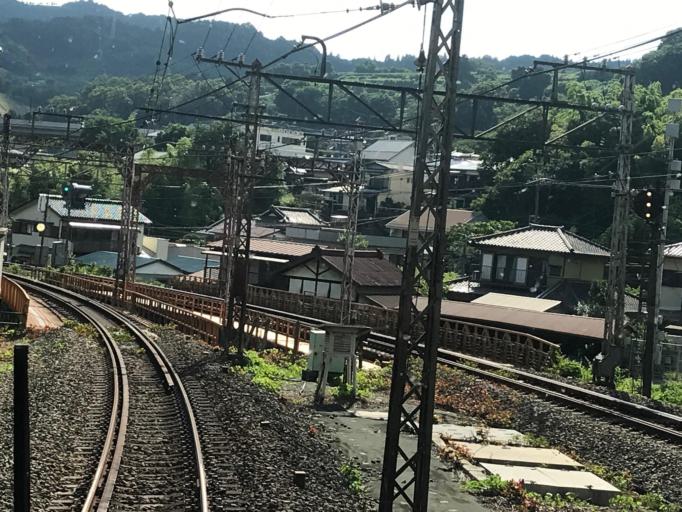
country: JP
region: Kanagawa
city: Hadano
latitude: 35.3744
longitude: 139.1756
